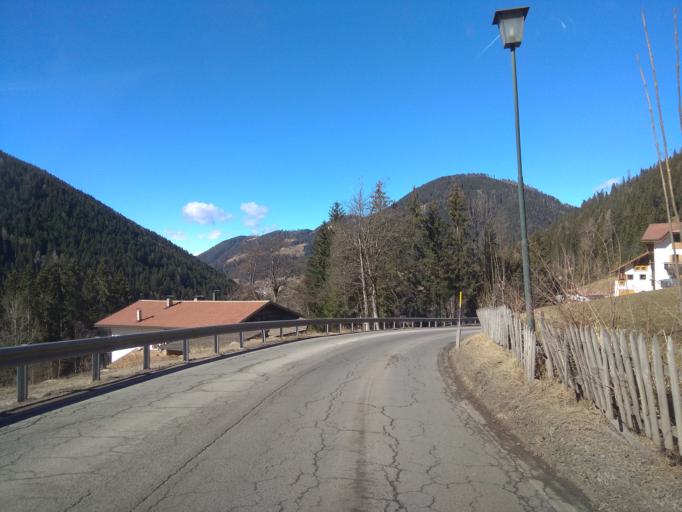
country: IT
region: Trentino-Alto Adige
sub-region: Bolzano
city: Nova Levante
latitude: 46.4221
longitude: 11.5564
